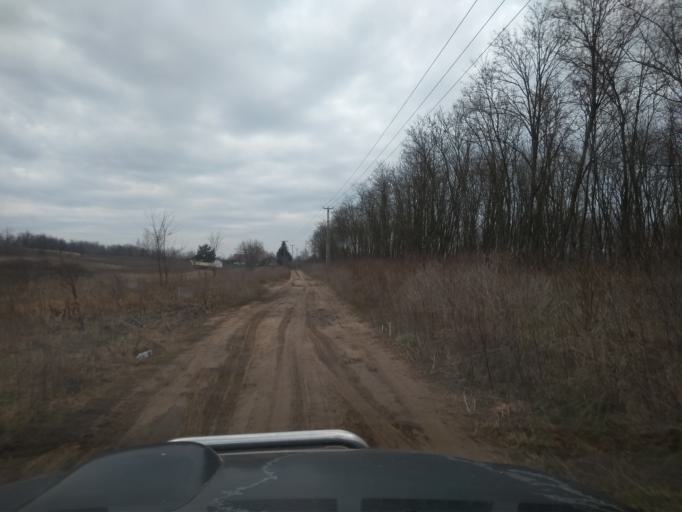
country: HU
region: Szabolcs-Szatmar-Bereg
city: Nyirpazony
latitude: 48.0172
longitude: 21.7886
